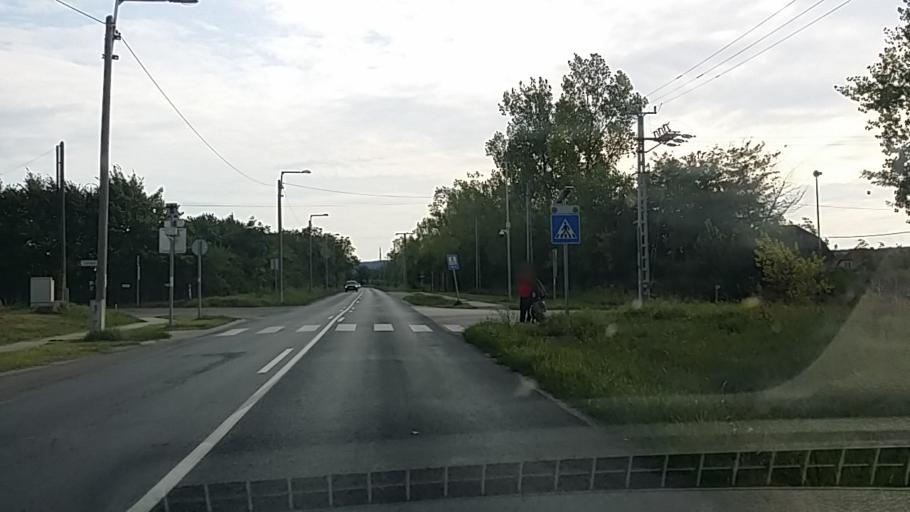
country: HU
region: Gyor-Moson-Sopron
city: Fertorakos
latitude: 47.7195
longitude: 16.6175
